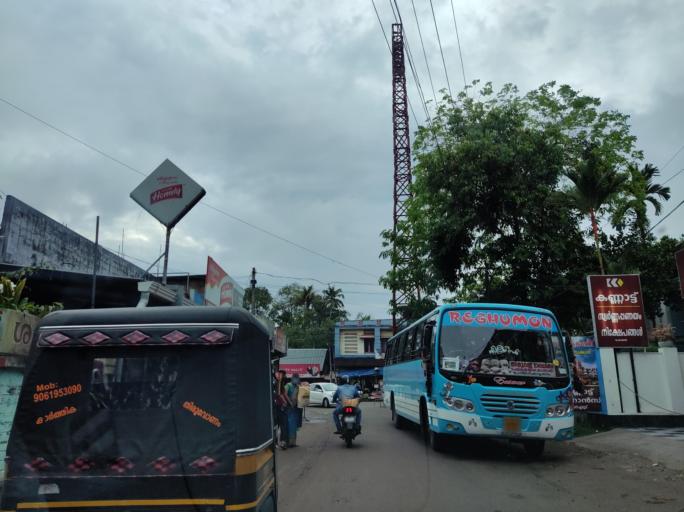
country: IN
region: Kerala
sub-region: Alappuzha
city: Mavelikara
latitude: 9.2418
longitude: 76.5202
